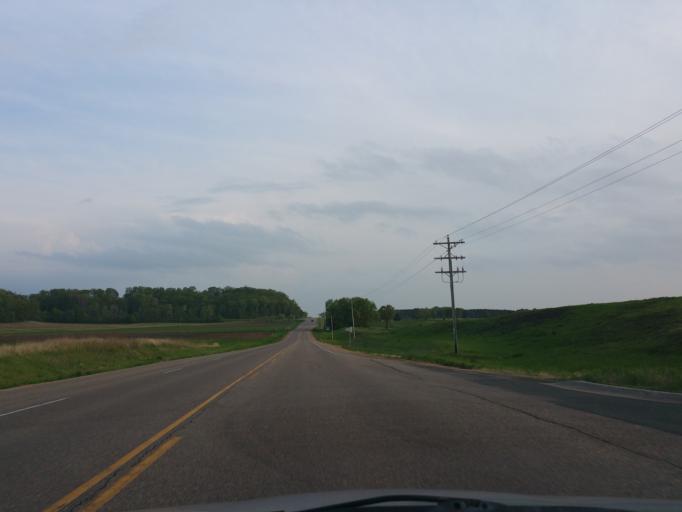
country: US
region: Minnesota
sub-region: Washington County
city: Lake Saint Croix Beach
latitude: 44.9060
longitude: -92.7316
